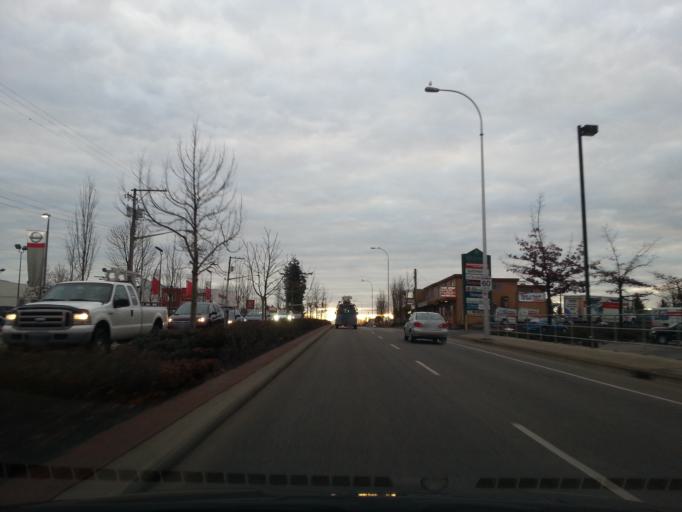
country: CA
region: British Columbia
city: Surrey
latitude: 49.1656
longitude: -122.8003
